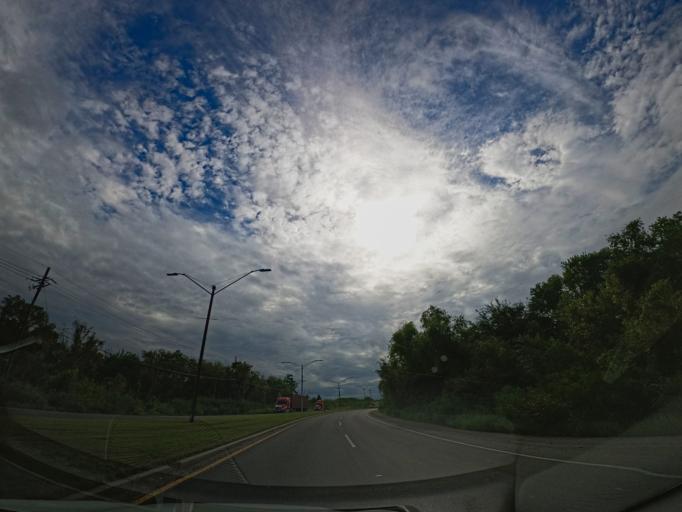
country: US
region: Louisiana
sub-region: Saint Bernard Parish
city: Chalmette
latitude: 30.0126
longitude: -89.9463
